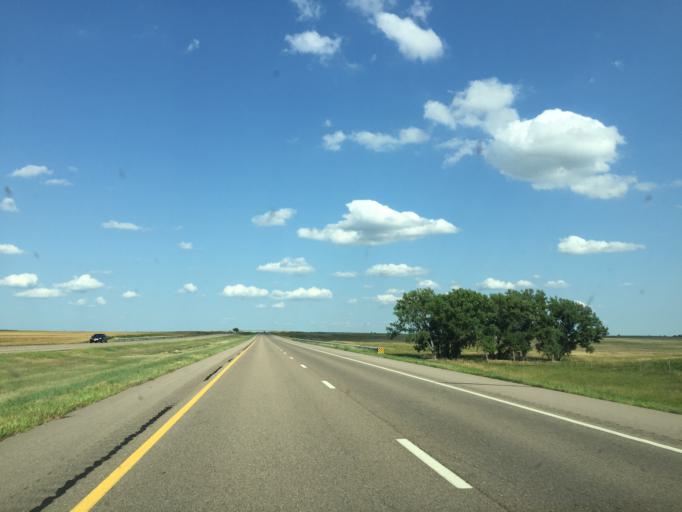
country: US
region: Kansas
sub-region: Trego County
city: WaKeeney
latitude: 39.0233
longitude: -100.0918
